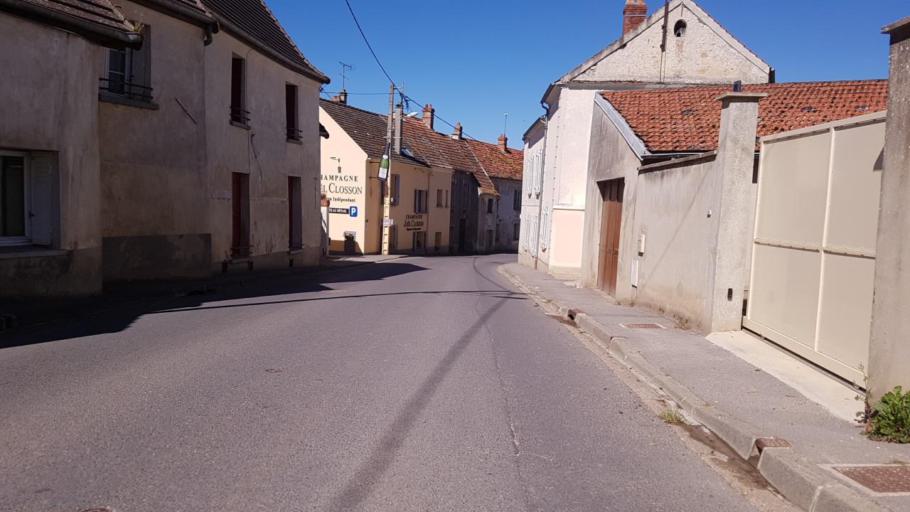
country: FR
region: Picardie
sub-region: Departement de l'Aisne
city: Charly-sur-Marne
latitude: 48.9753
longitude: 3.3062
